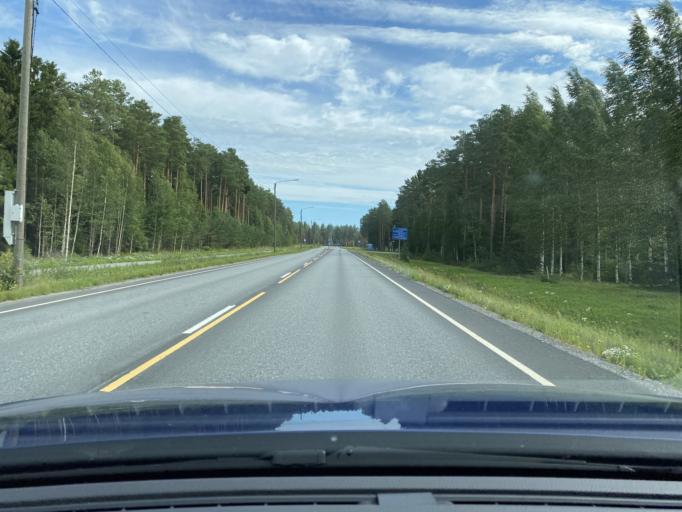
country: FI
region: Southern Ostrobothnia
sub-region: Seinaejoki
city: Ylihaermae
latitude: 63.1419
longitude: 22.8192
